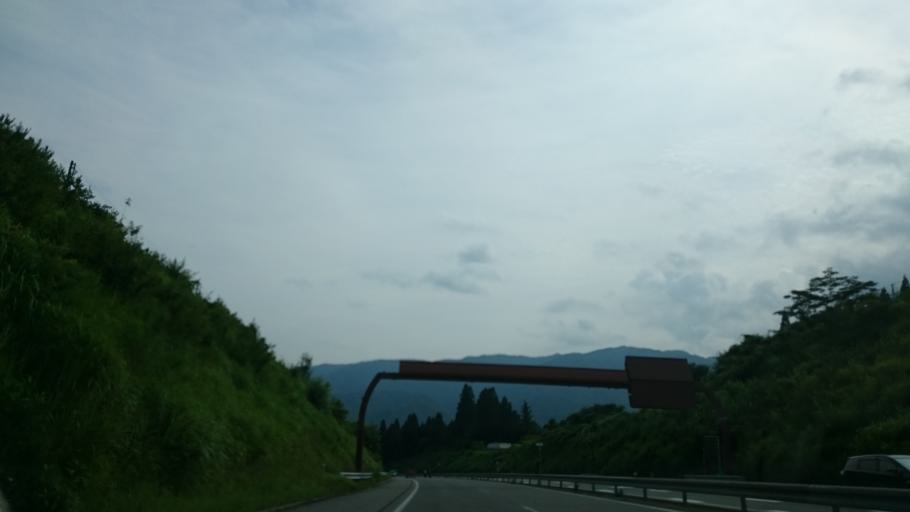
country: JP
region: Gifu
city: Gujo
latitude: 35.8682
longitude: 136.8711
